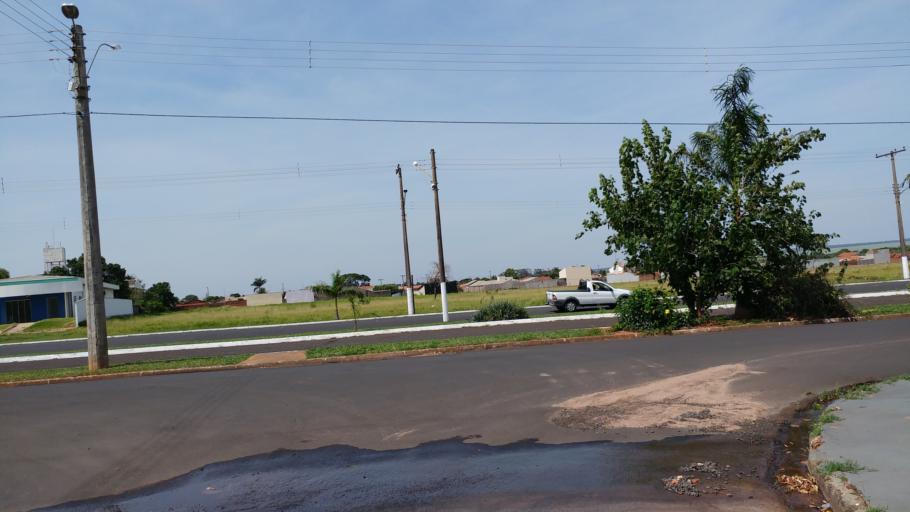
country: BR
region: Sao Paulo
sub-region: Paraguacu Paulista
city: Paraguacu Paulista
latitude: -22.4107
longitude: -50.5885
